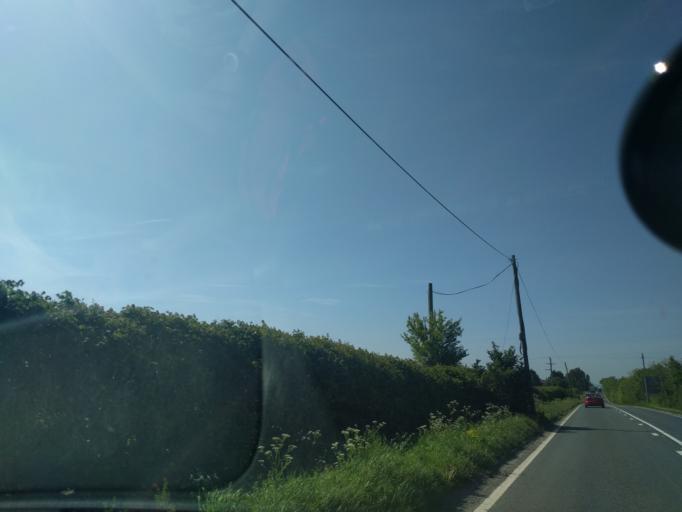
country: GB
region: England
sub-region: Somerset
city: Ilchester
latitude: 51.0434
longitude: -2.6527
